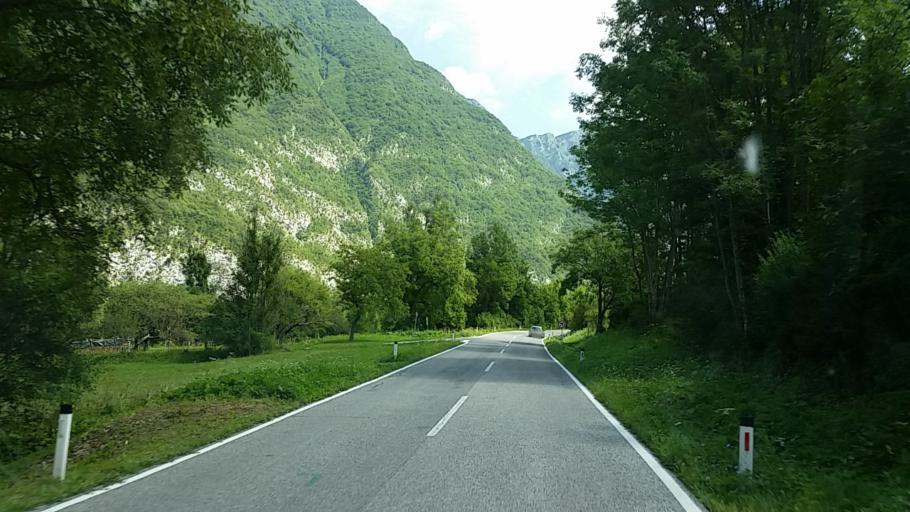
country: SI
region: Bovec
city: Bovec
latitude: 46.2887
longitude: 13.5022
